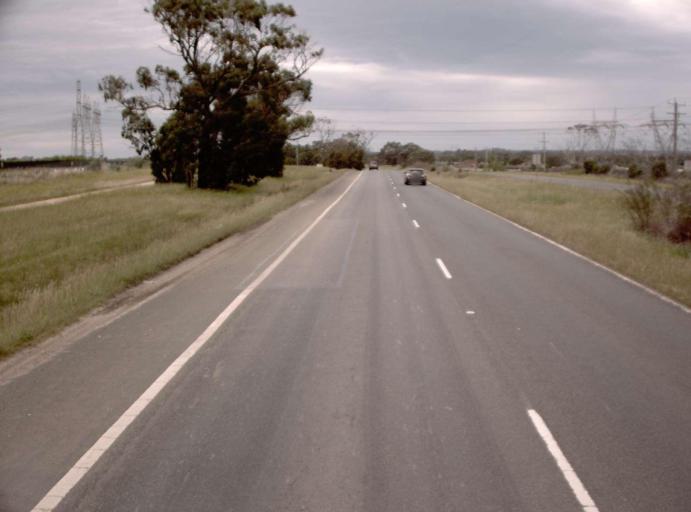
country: AU
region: Victoria
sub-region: Casey
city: Lynbrook
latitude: -38.0609
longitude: 145.2640
